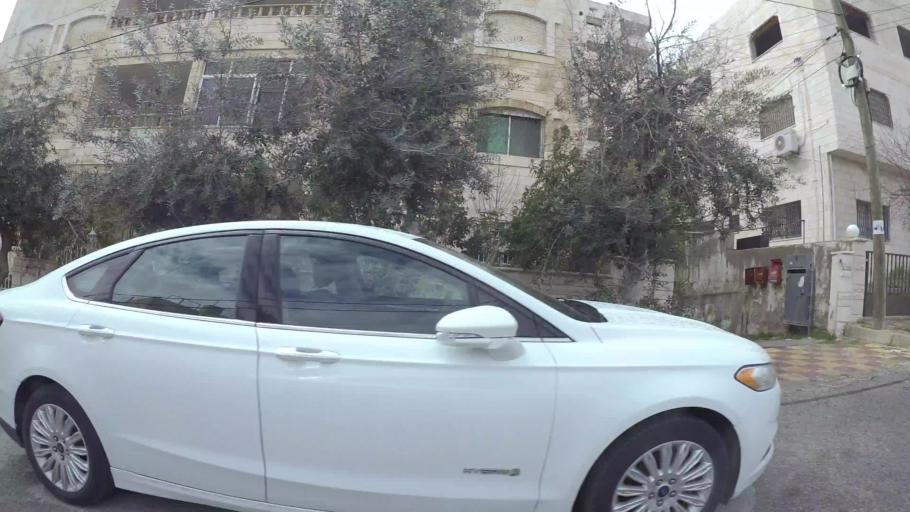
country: JO
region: Amman
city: Al Jubayhah
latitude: 31.9939
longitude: 35.8576
